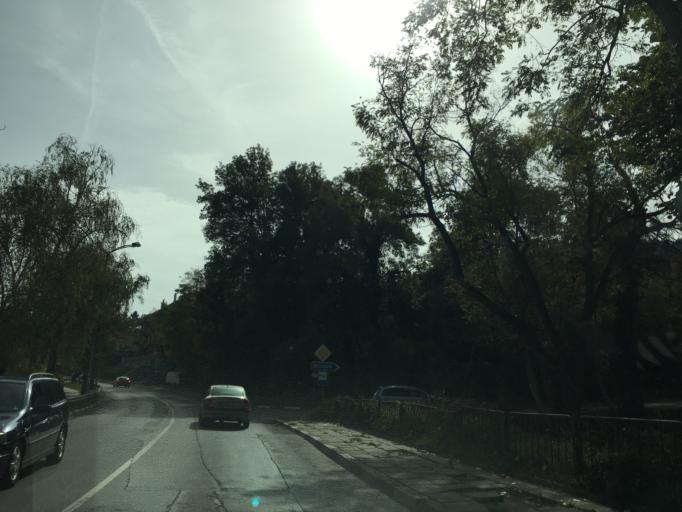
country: BG
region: Sofia-Capital
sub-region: Stolichna Obshtina
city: Sofia
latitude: 42.5999
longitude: 23.4040
